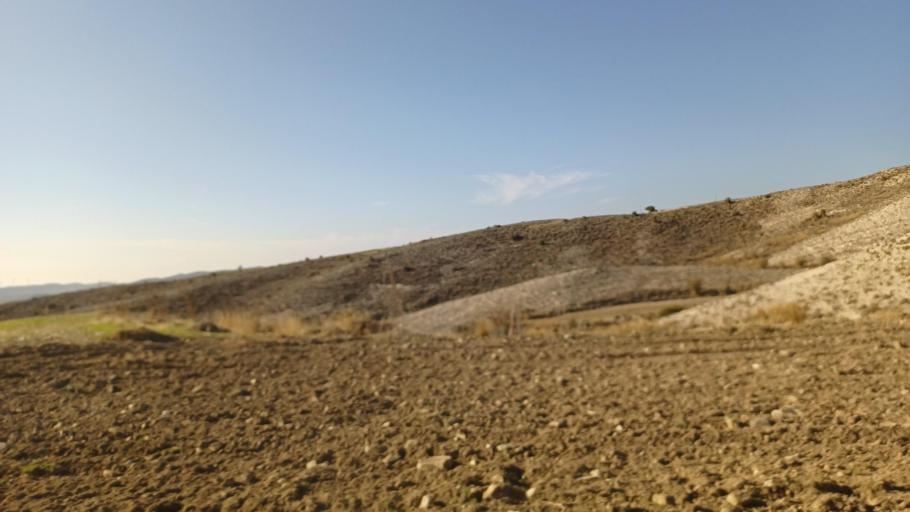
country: CY
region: Larnaka
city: Psevdas
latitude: 34.9458
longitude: 33.5176
